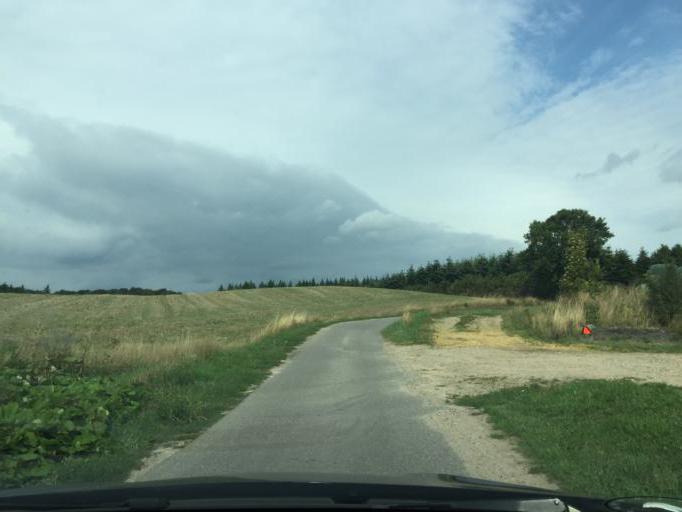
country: DK
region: South Denmark
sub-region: Assens Kommune
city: Vissenbjerg
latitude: 55.4110
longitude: 10.1967
